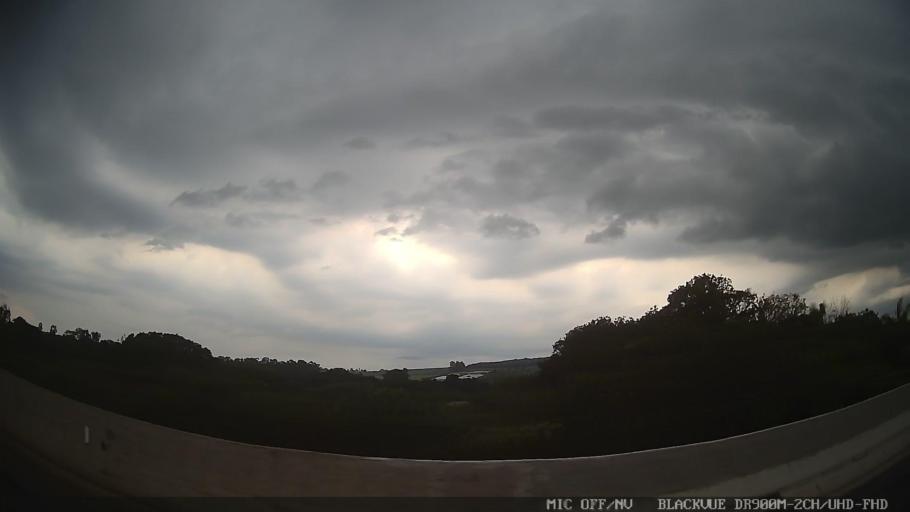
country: BR
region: Sao Paulo
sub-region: Jarinu
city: Jarinu
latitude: -23.0398
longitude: -46.6800
